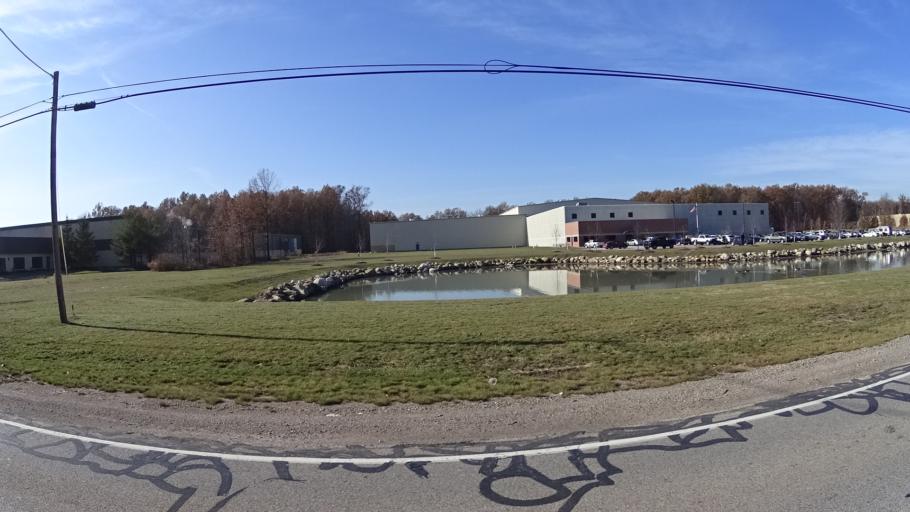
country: US
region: Ohio
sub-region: Lorain County
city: Avon Center
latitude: 41.4711
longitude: -81.9994
